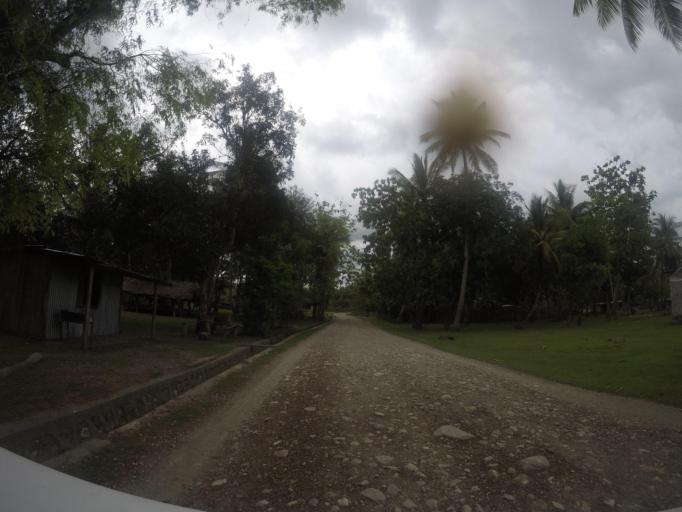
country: TL
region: Viqueque
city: Viqueque
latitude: -8.8602
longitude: 126.3592
